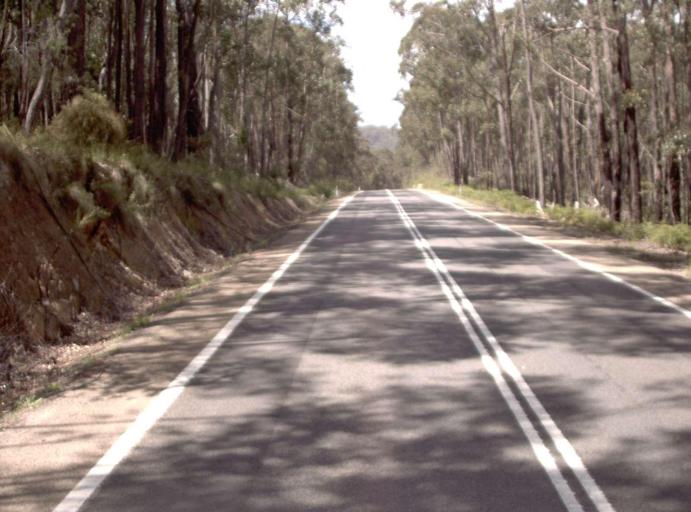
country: AU
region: New South Wales
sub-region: Bombala
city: Bombala
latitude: -37.5667
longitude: 149.3237
